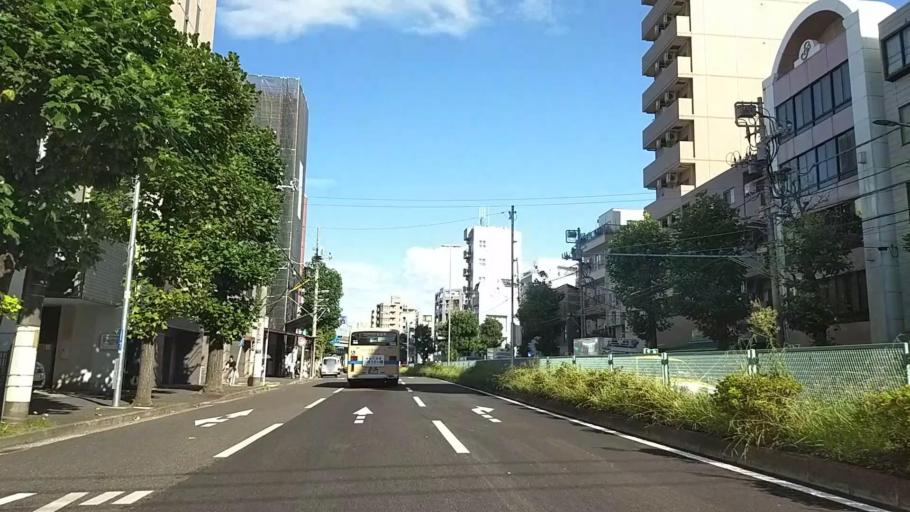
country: JP
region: Kanagawa
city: Yokohama
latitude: 35.4811
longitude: 139.6310
